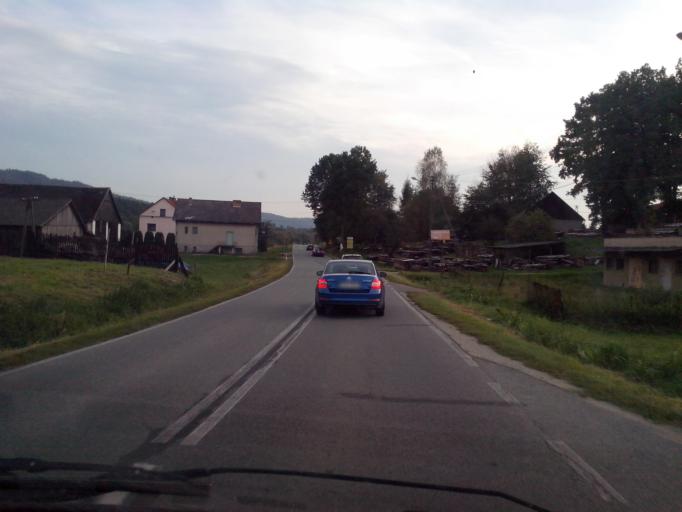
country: PL
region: Subcarpathian Voivodeship
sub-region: Powiat strzyzowski
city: Jawornik
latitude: 49.8069
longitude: 21.8723
